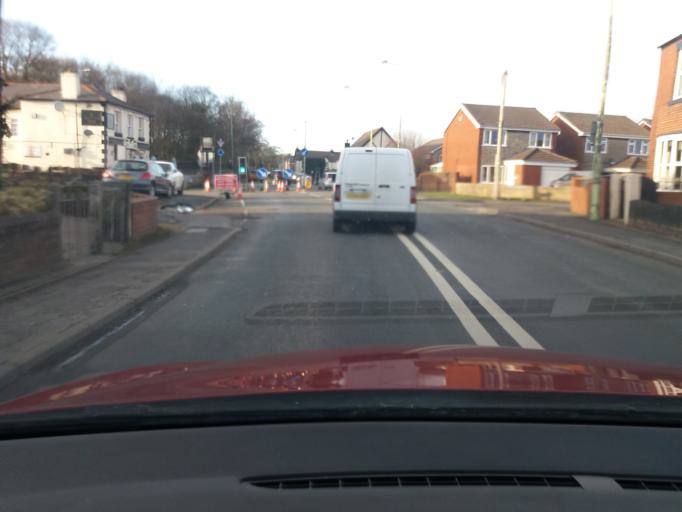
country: GB
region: England
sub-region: Lancashire
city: Euxton
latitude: 53.6584
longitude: -2.6741
